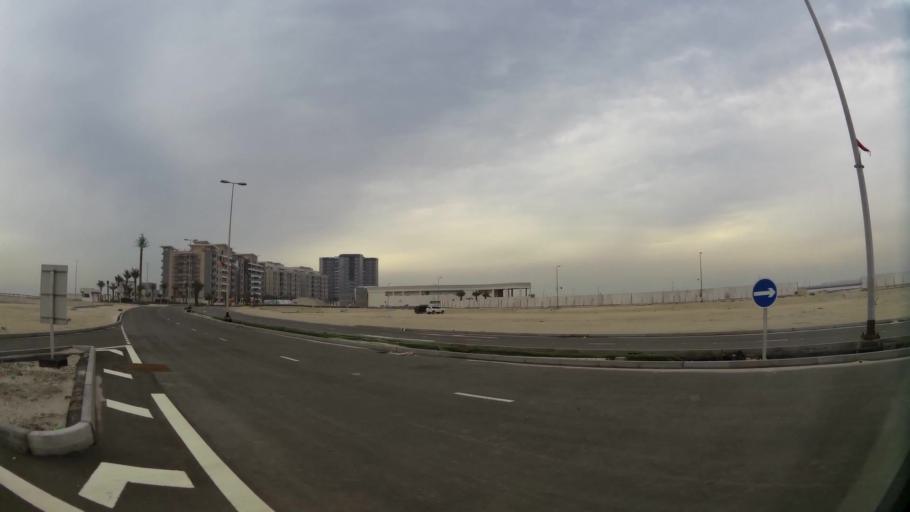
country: BH
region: Central Governorate
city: Dar Kulayb
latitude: 25.8675
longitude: 50.6058
